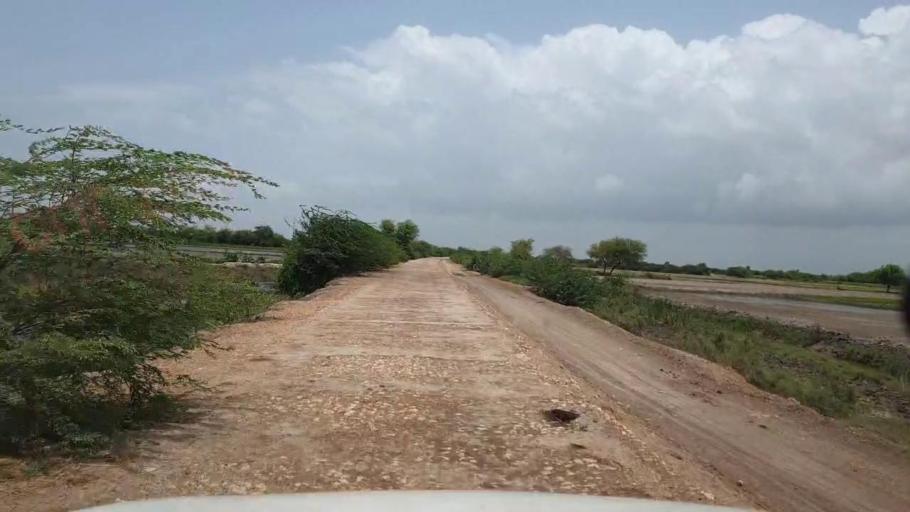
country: PK
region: Sindh
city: Kario
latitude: 24.6930
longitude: 68.6532
